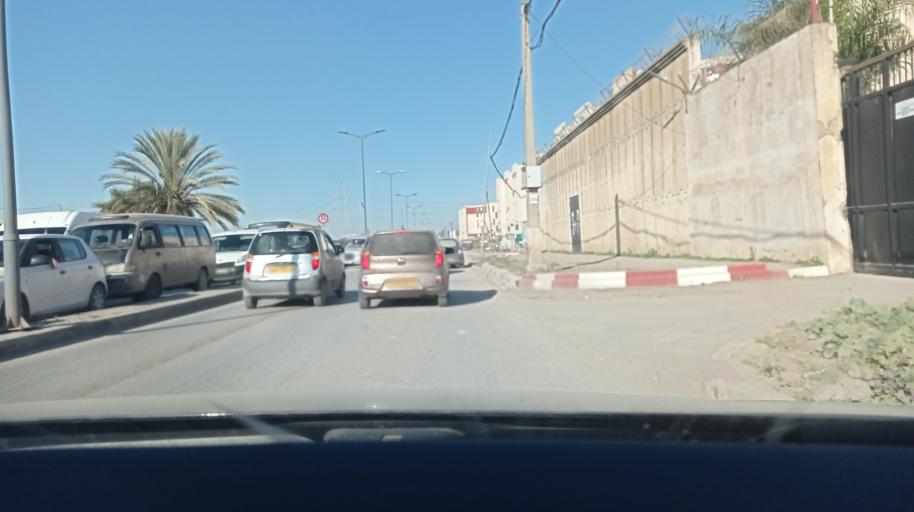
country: DZ
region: Tipaza
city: Baraki
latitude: 36.6608
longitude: 3.0854
